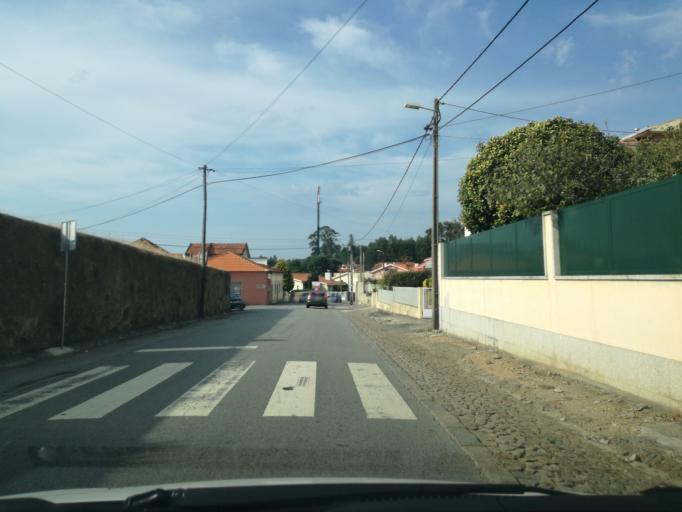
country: PT
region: Porto
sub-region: Vila Nova de Gaia
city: Azenha
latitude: 41.0680
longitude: -8.6272
